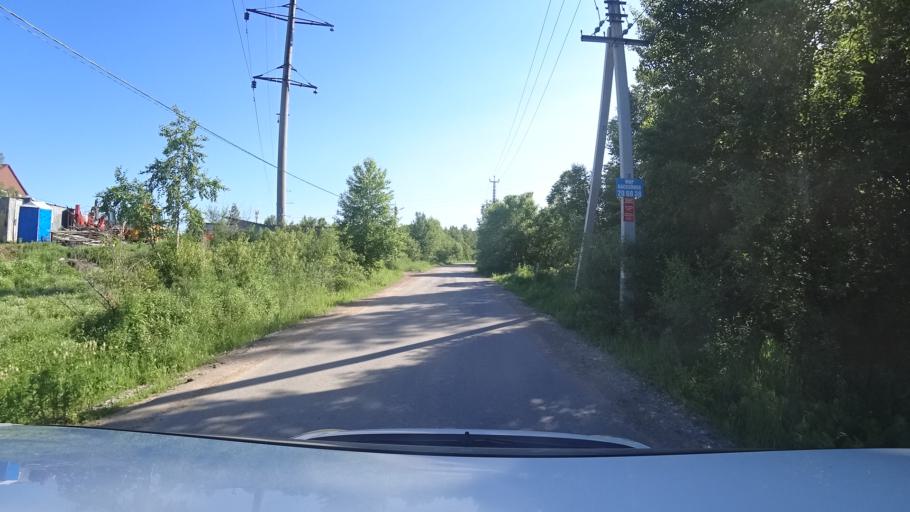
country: RU
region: Khabarovsk Krai
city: Topolevo
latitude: 48.5468
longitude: 135.1851
